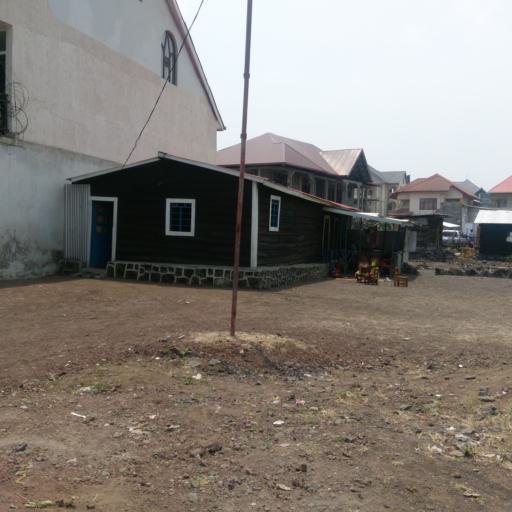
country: CD
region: Nord Kivu
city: Goma
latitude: -1.6955
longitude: 29.2348
